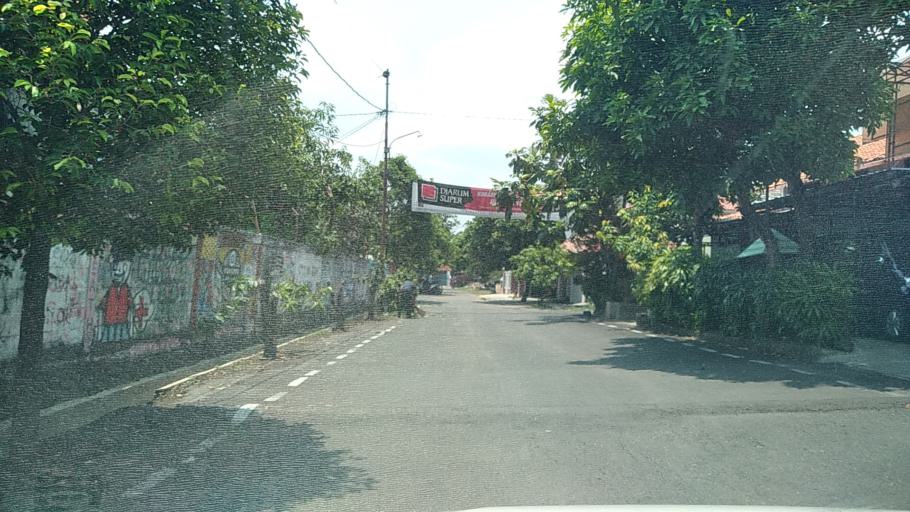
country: ID
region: Central Java
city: Semarang
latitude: -7.0056
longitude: 110.4457
